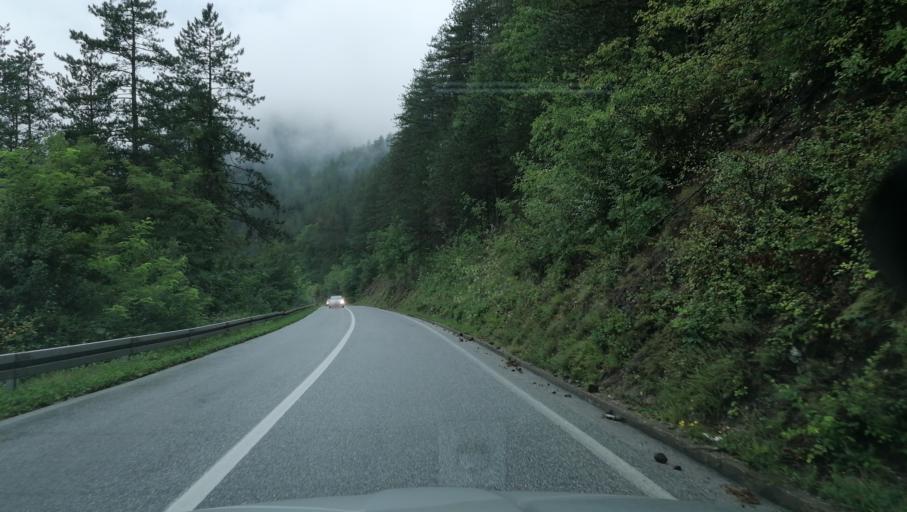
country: BA
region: Republika Srpska
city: Visegrad
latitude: 43.7817
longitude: 19.3486
